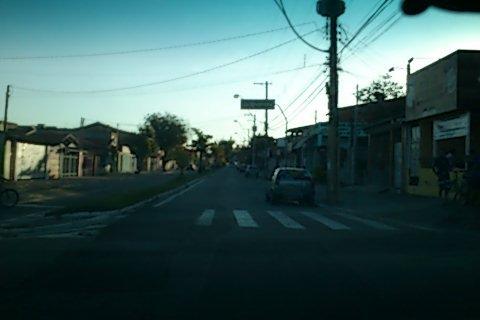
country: BR
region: Sao Paulo
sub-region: Sao Jose Dos Campos
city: Sao Jose dos Campos
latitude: -23.1662
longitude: -45.9112
